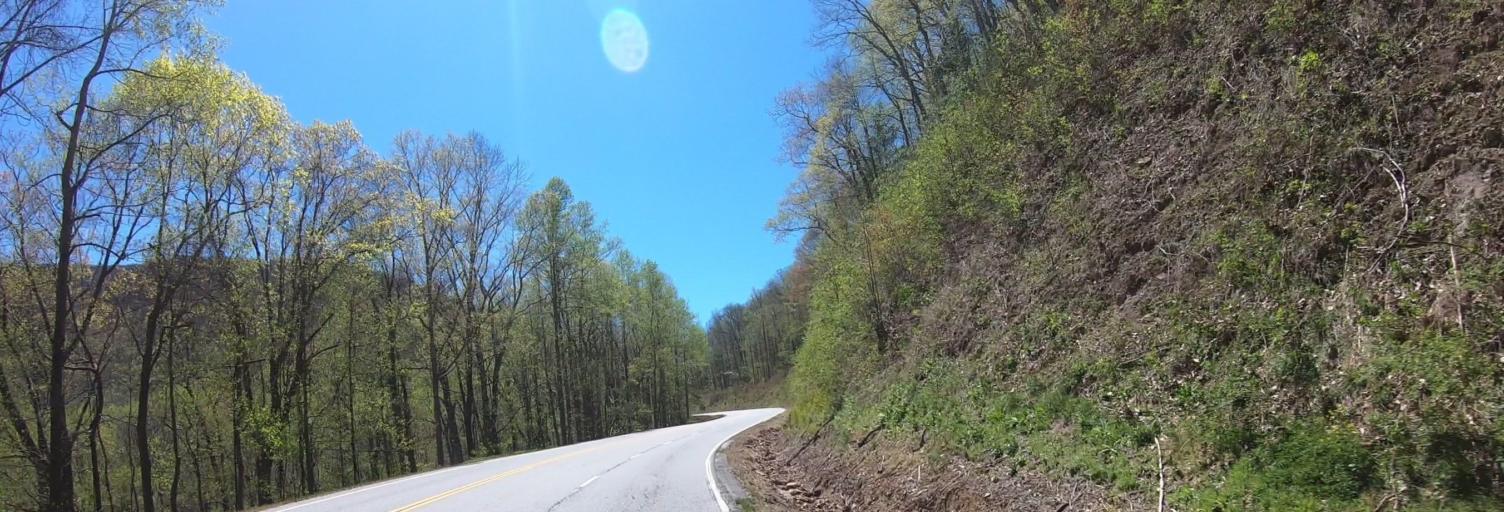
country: US
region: Georgia
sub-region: Towns County
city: Hiawassee
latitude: 34.8067
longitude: -83.7435
